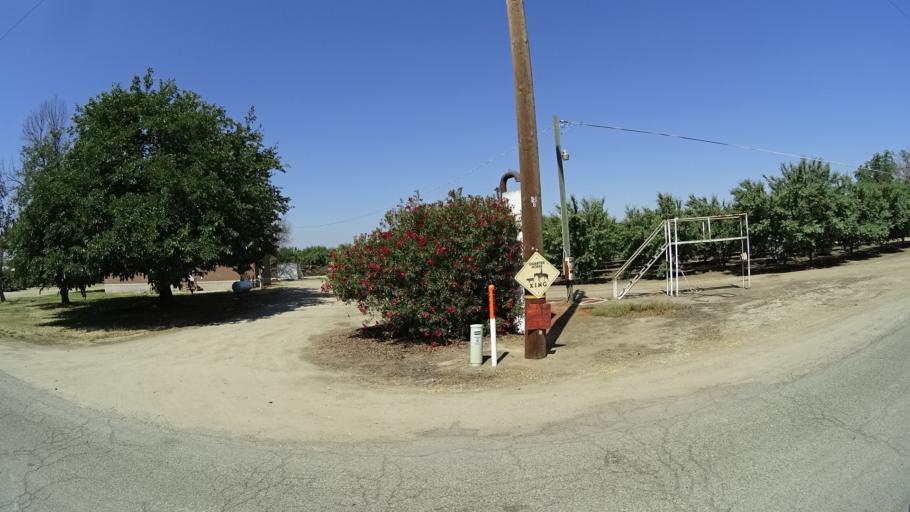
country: US
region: California
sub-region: Fresno County
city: Kingsburg
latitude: 36.4482
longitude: -119.5825
